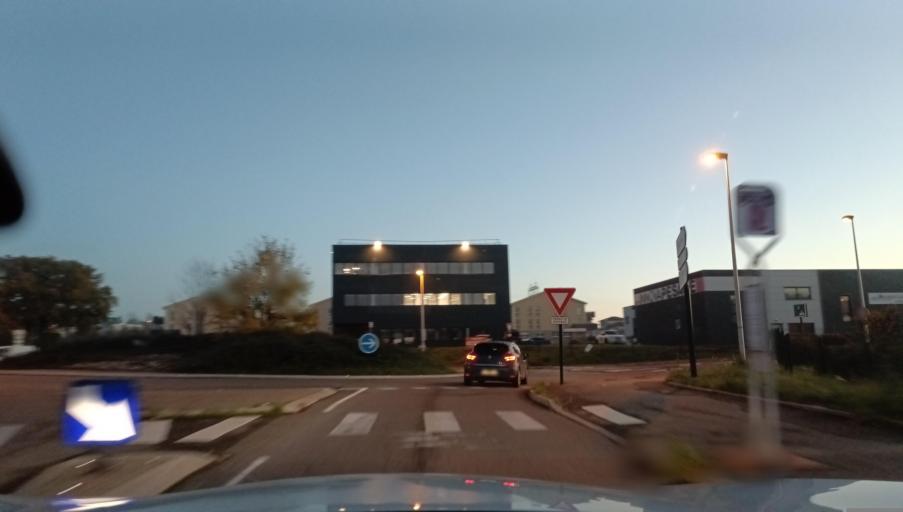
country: FR
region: Rhone-Alpes
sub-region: Departement de l'Isere
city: Chasse-sur-Rhone
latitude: 45.5874
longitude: 4.8126
